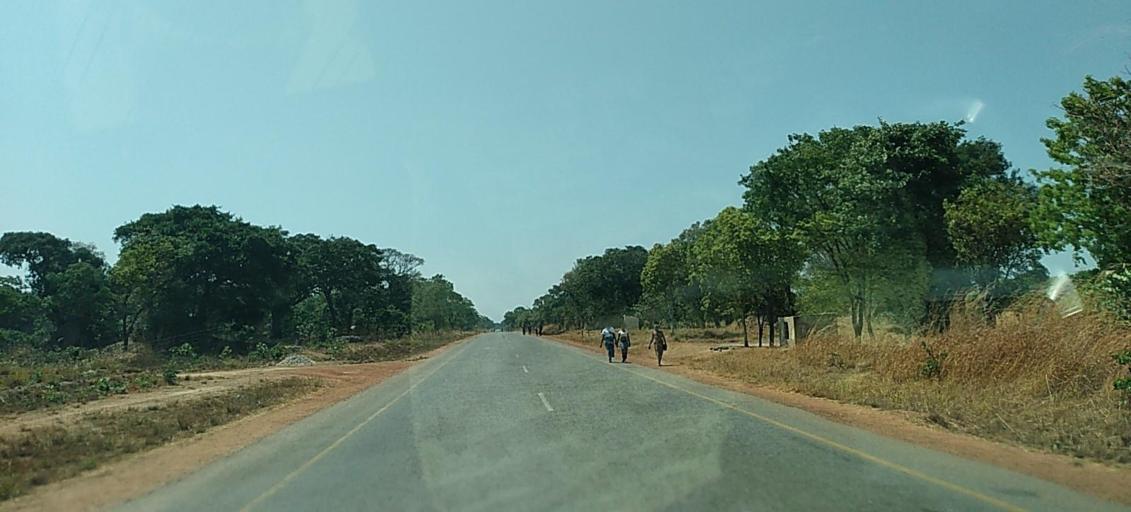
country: ZM
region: North-Western
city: Solwezi
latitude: -12.2872
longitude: 25.6920
